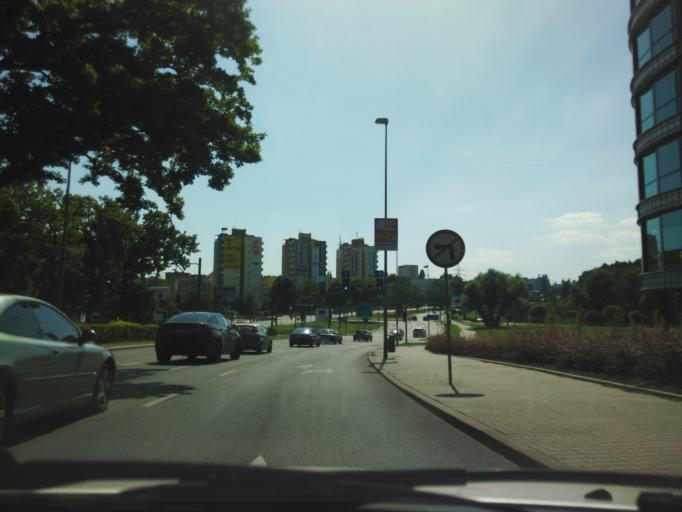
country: PL
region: West Pomeranian Voivodeship
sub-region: Szczecin
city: Szczecin
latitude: 53.4179
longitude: 14.5324
